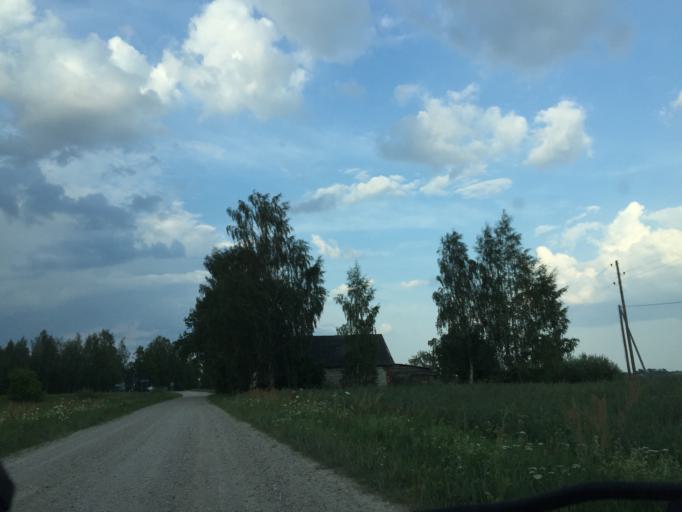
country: LV
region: Dobeles Rajons
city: Dobele
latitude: 56.6189
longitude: 23.3700
